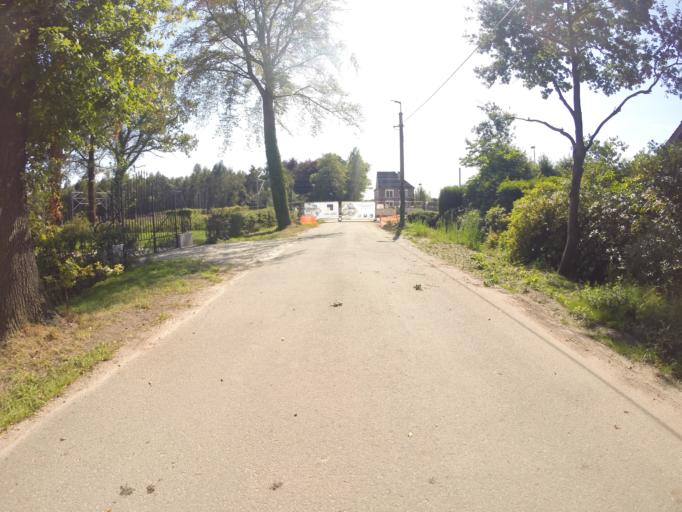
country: BE
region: Flanders
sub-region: Provincie Oost-Vlaanderen
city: Aalter
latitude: 51.0841
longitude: 3.4888
